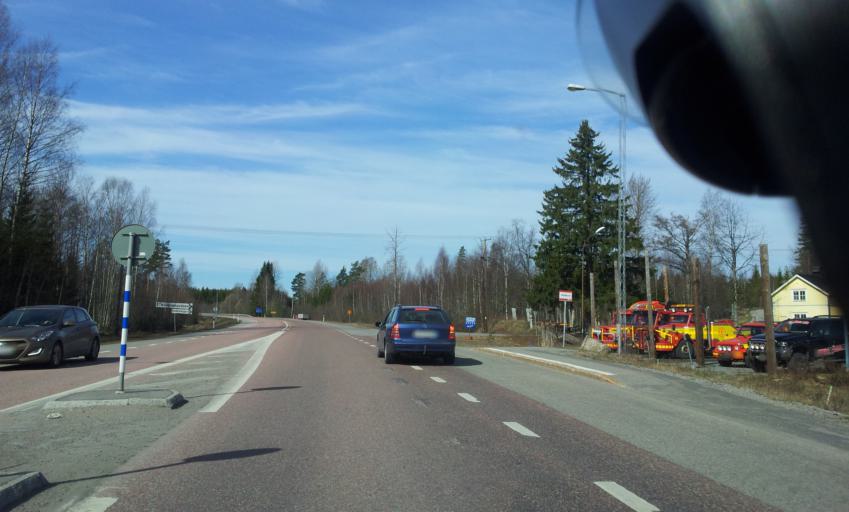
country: SE
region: Gaevleborg
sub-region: Hudiksvalls Kommun
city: Hudiksvall
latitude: 61.7145
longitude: 17.0645
